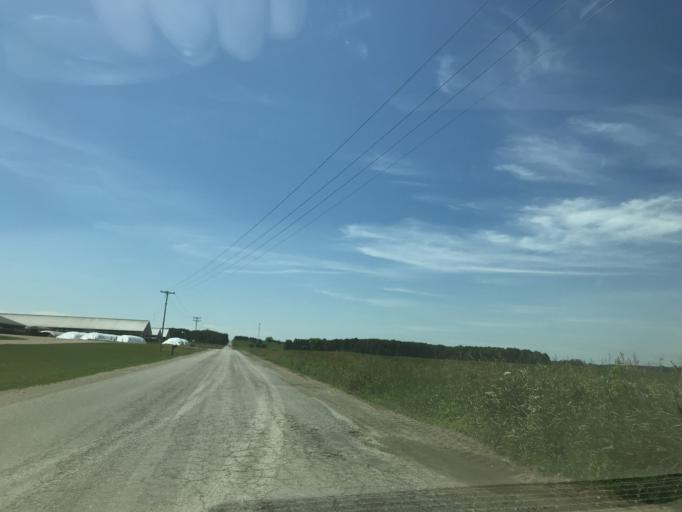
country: US
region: Michigan
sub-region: Missaukee County
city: Lake City
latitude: 44.3121
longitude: -85.0747
